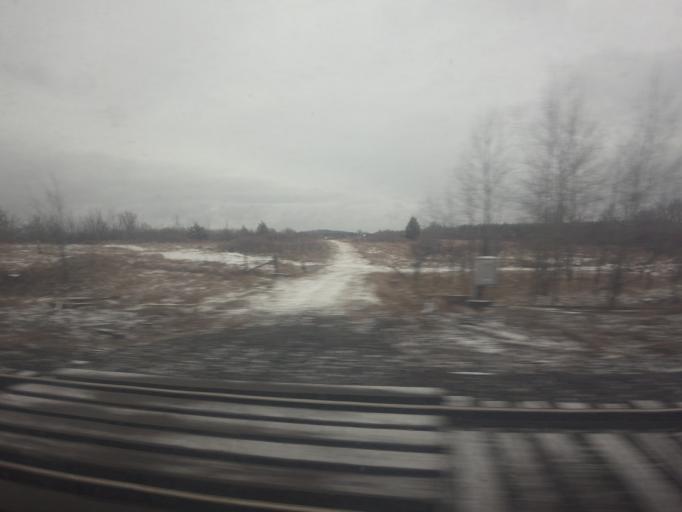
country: CA
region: Ontario
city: Gananoque
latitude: 44.3731
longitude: -76.1143
